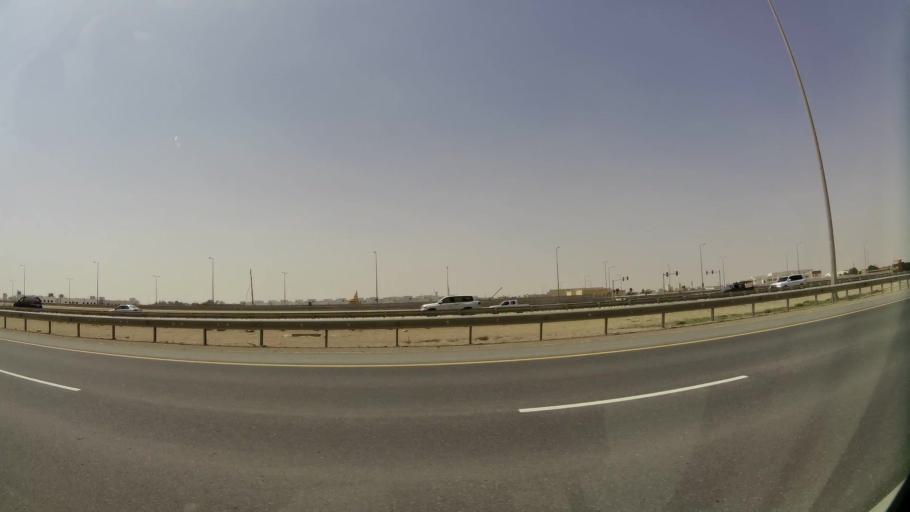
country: QA
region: Baladiyat Umm Salal
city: Umm Salal Muhammad
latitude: 25.4169
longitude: 51.4217
